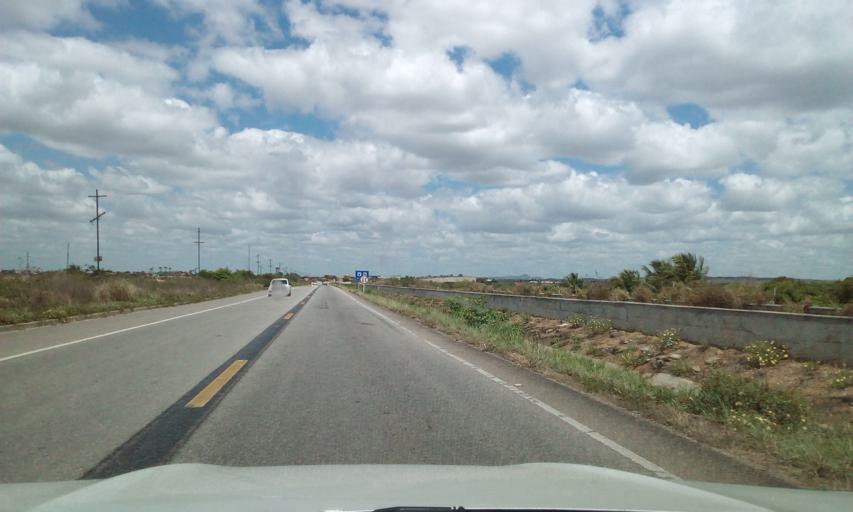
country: BR
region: Alagoas
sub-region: Porto Real Do Colegio
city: Porto Real do Colegio
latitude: -10.1932
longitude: -36.8245
